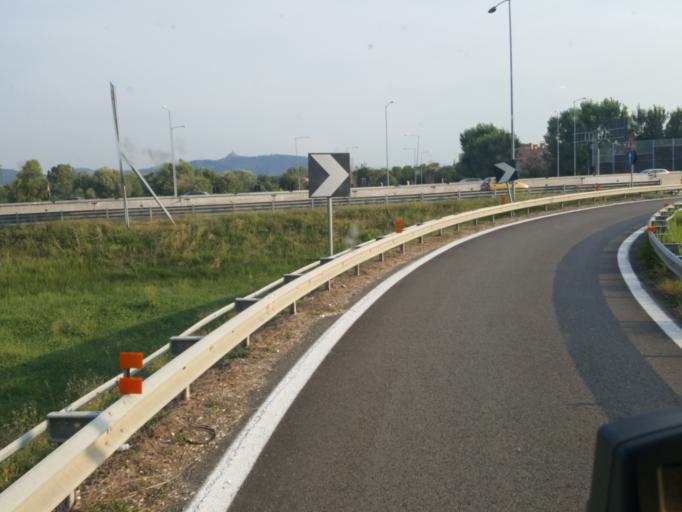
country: IT
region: Emilia-Romagna
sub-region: Provincia di Bologna
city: Trebbo
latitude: 44.5252
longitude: 11.2987
